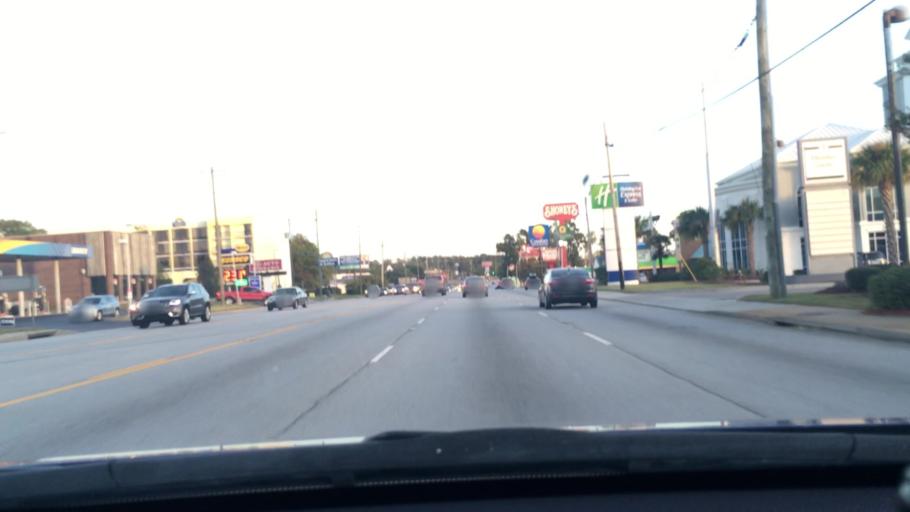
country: US
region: South Carolina
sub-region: Richland County
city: Forest Acres
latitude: 33.9714
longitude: -80.9508
